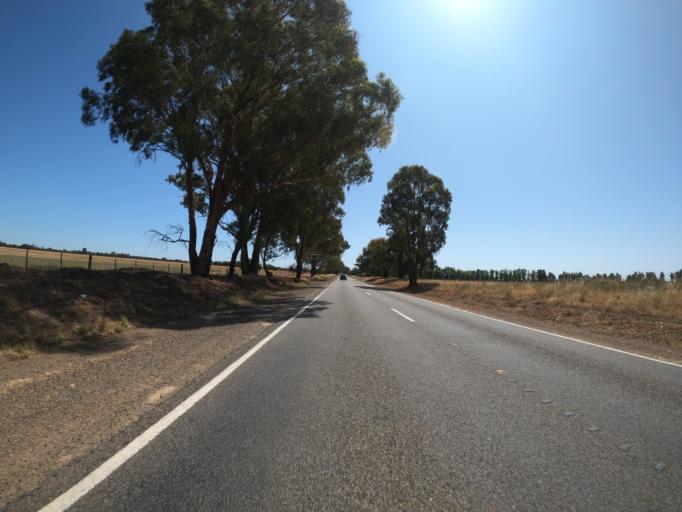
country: AU
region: Victoria
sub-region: Moira
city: Yarrawonga
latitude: -36.0253
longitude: 146.0997
